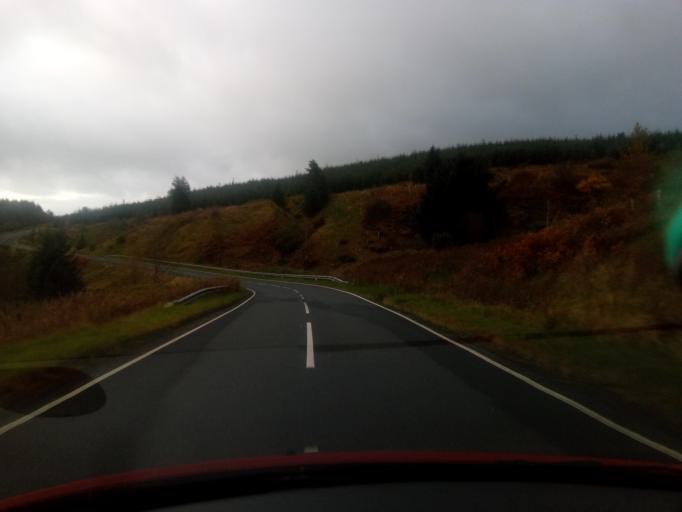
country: GB
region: Scotland
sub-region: The Scottish Borders
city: Hawick
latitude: 55.3121
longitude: -2.6559
